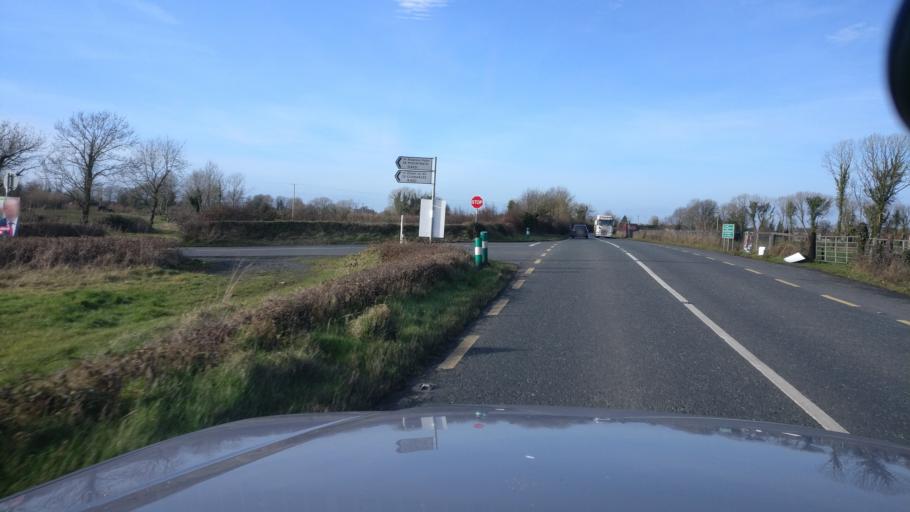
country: IE
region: Leinster
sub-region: Laois
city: Mountmellick
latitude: 53.1469
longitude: -7.3681
